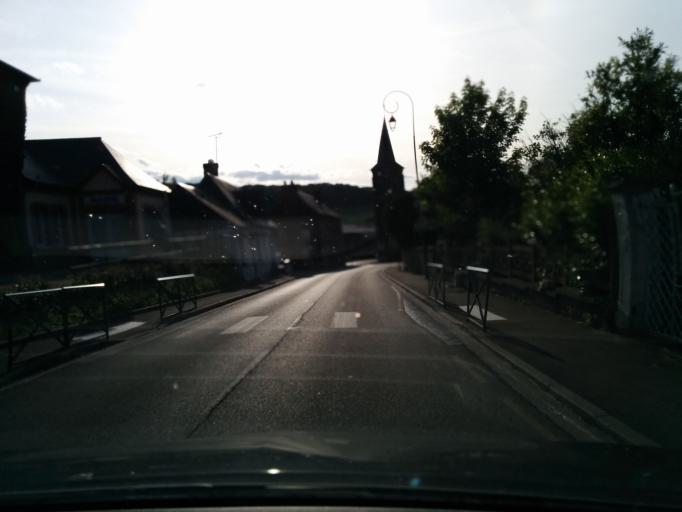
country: FR
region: Haute-Normandie
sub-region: Departement de la Seine-Maritime
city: La Feuillie
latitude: 49.4936
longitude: 1.4819
